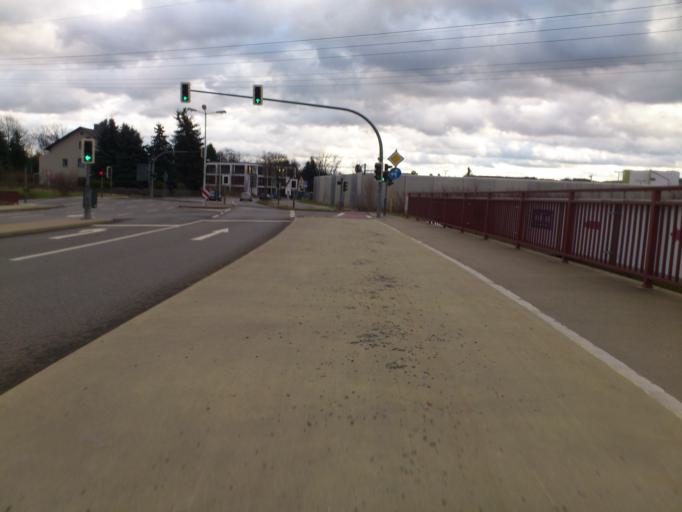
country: DE
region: Saxony
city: Chemnitz
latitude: 50.8025
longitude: 12.9397
